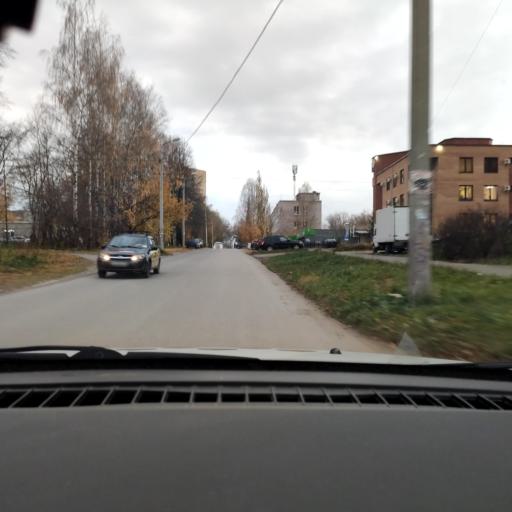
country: RU
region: Perm
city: Perm
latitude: 58.1097
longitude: 56.3826
